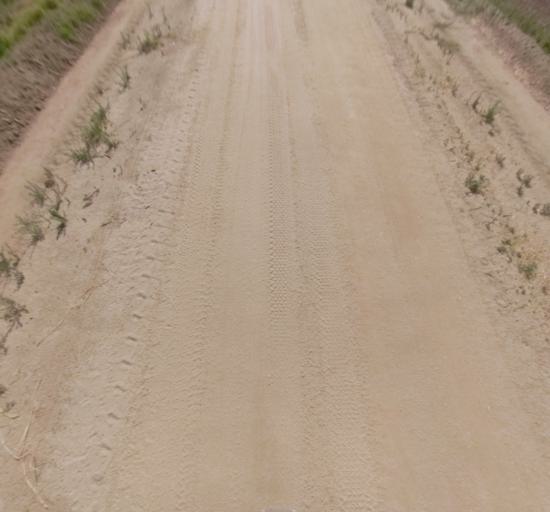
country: US
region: California
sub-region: Madera County
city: Chowchilla
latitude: 37.0108
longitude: -120.3681
